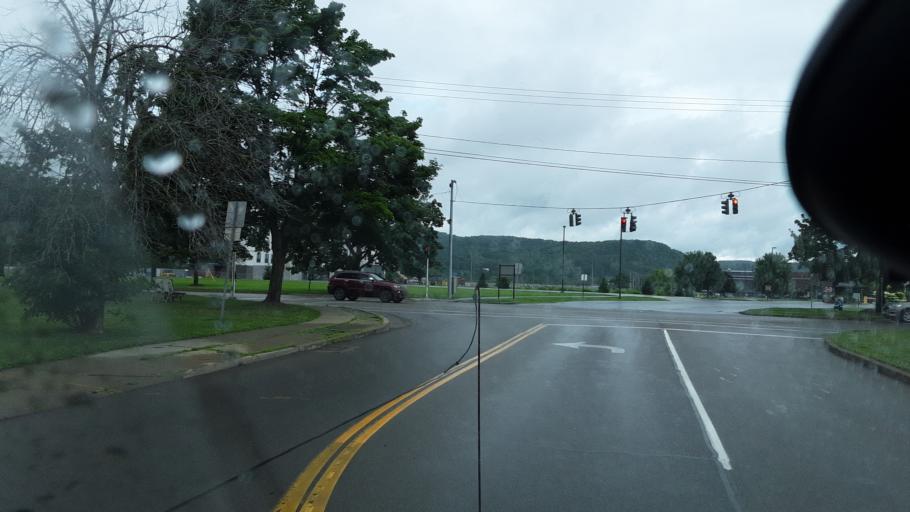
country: US
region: New York
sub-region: Cattaraugus County
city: Olean
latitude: 42.0847
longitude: -78.4448
